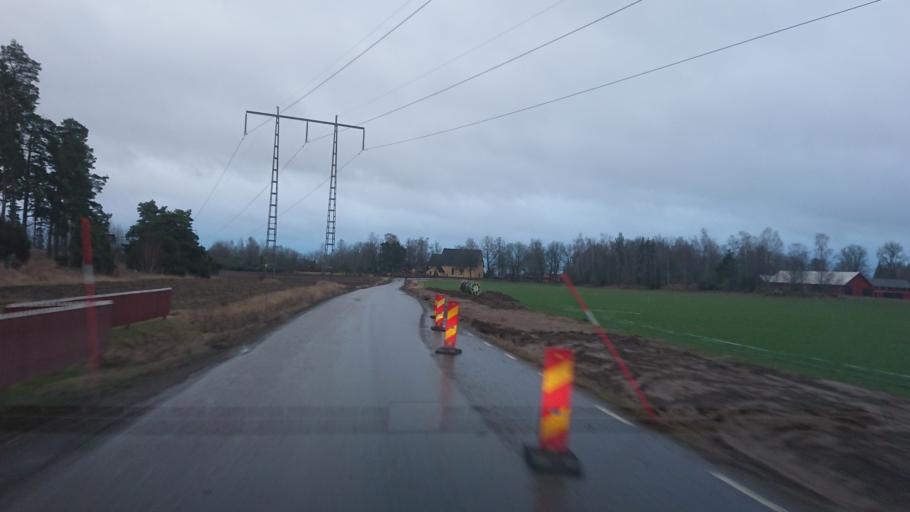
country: SE
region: Uppsala
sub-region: Uppsala Kommun
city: Gamla Uppsala
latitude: 59.9590
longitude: 17.6051
